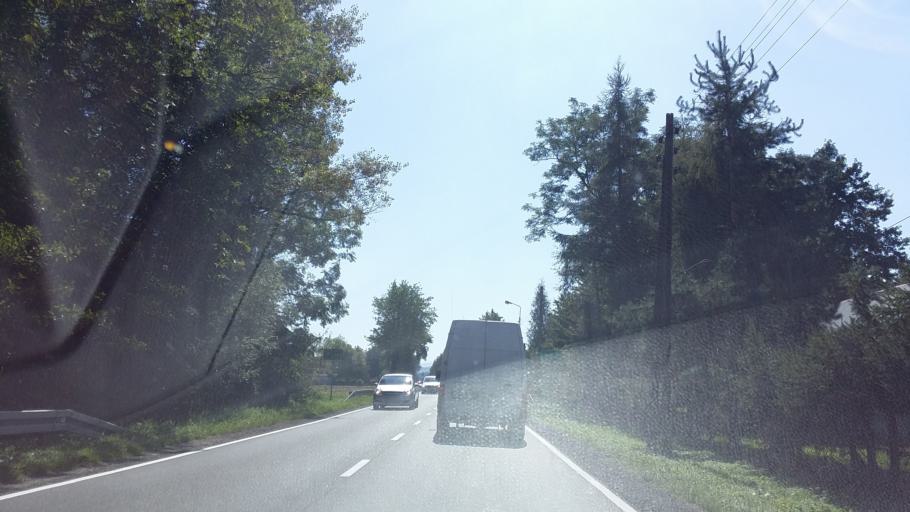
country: PL
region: Lesser Poland Voivodeship
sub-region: Powiat oswiecimski
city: Zator
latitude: 49.9799
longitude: 19.4388
